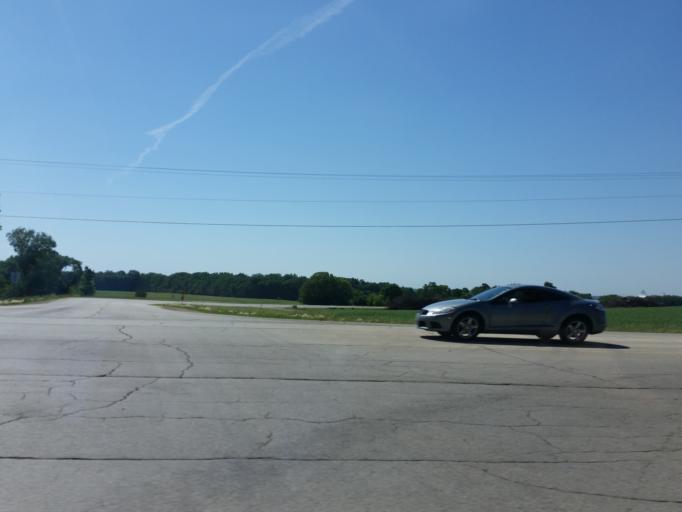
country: US
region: Illinois
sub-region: Ogle County
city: Davis Junction
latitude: 42.1671
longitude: -89.0742
